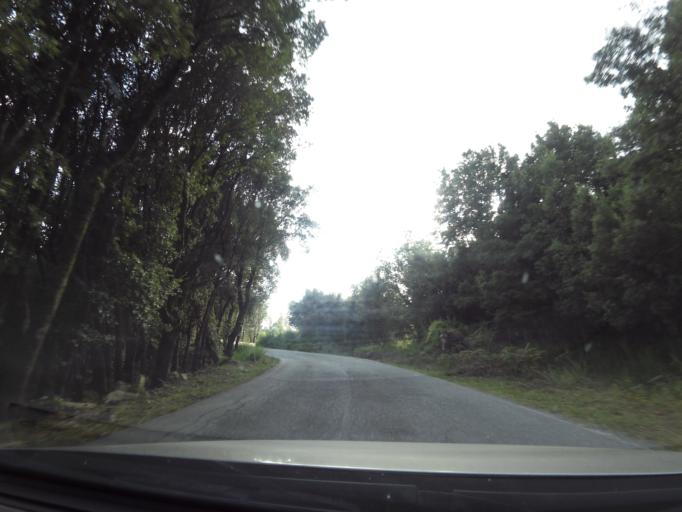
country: IT
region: Calabria
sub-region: Provincia di Vibo-Valentia
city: Nardodipace
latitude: 38.4779
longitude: 16.3912
